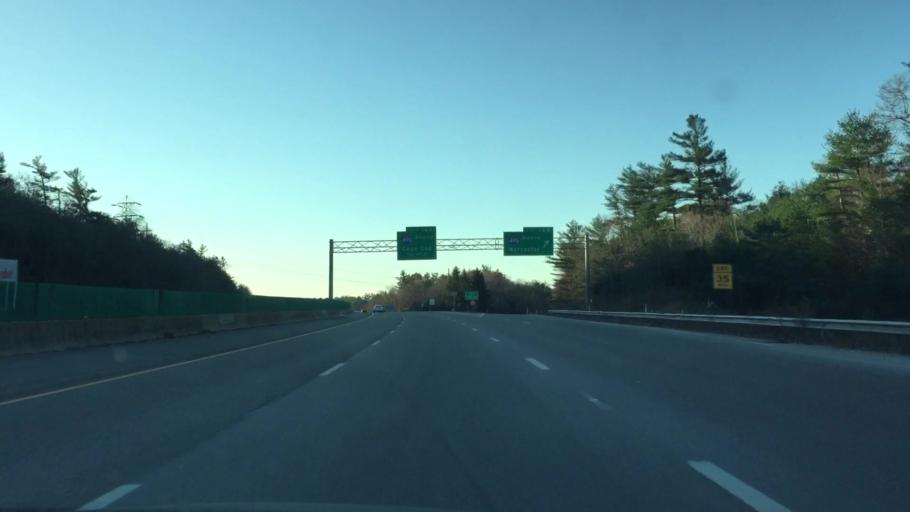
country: US
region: Massachusetts
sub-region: Bristol County
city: Raynham Center
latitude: 41.9615
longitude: -71.0283
